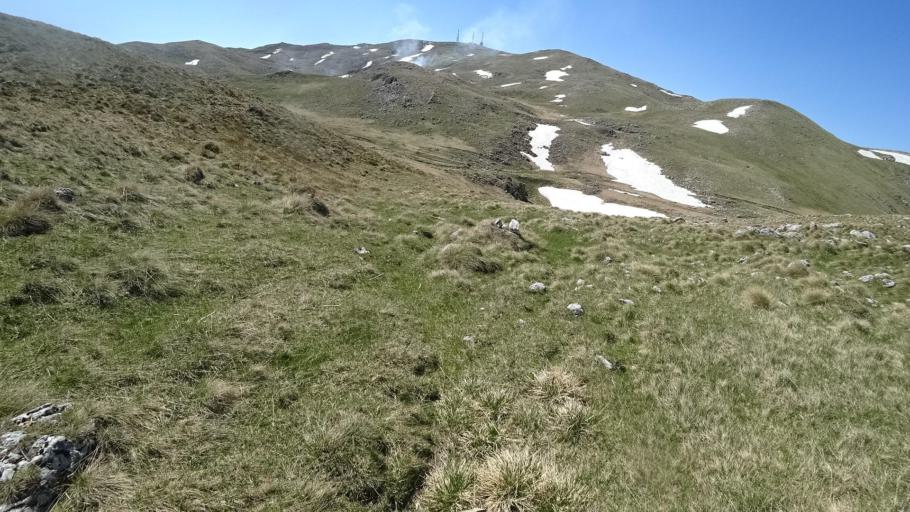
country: BA
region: Federation of Bosnia and Herzegovina
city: Travnik
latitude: 44.2873
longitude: 17.6529
